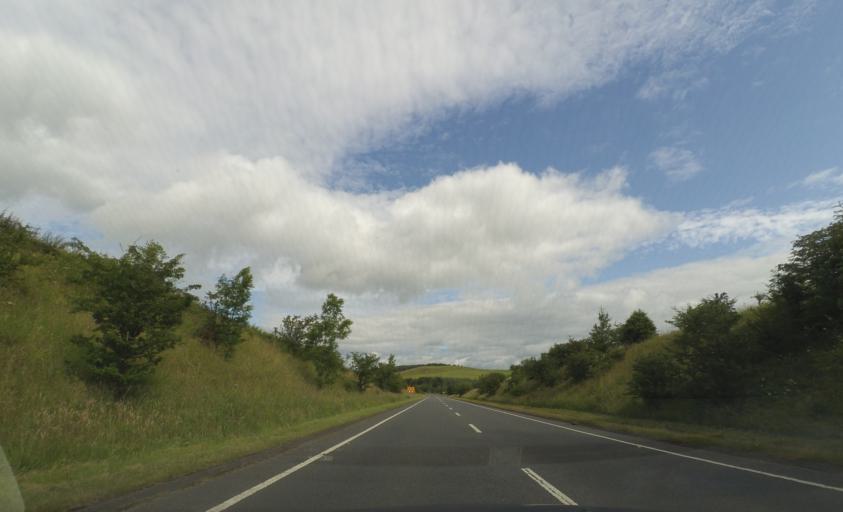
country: GB
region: Scotland
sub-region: The Scottish Borders
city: Selkirk
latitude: 55.5305
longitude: -2.8266
